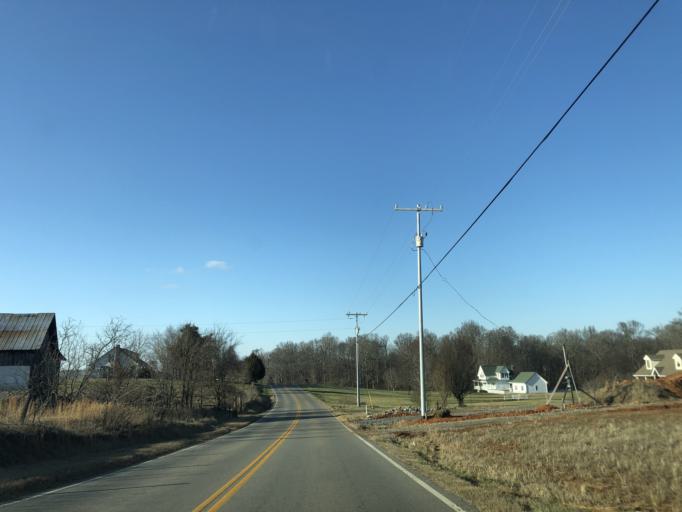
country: US
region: Tennessee
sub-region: Sumner County
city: White House
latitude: 36.4827
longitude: -86.5787
